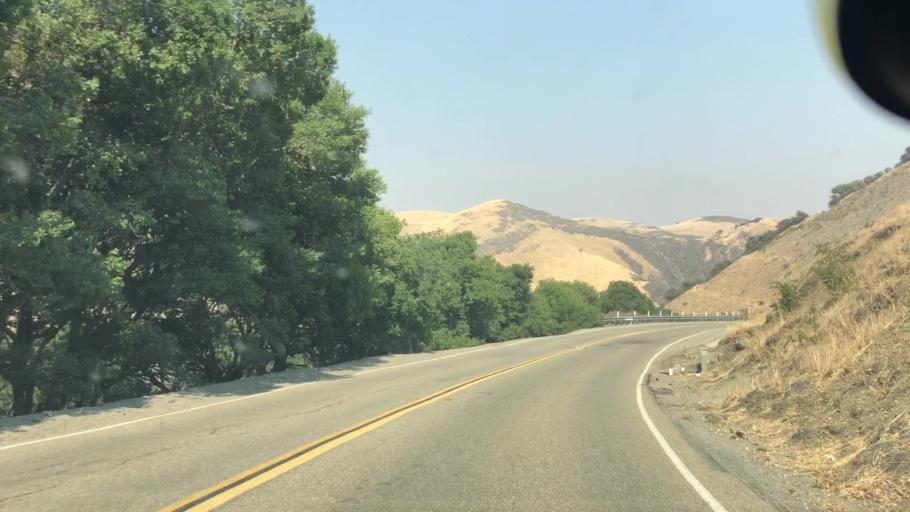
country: US
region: California
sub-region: San Joaquin County
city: Mountain House
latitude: 37.6508
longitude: -121.6076
